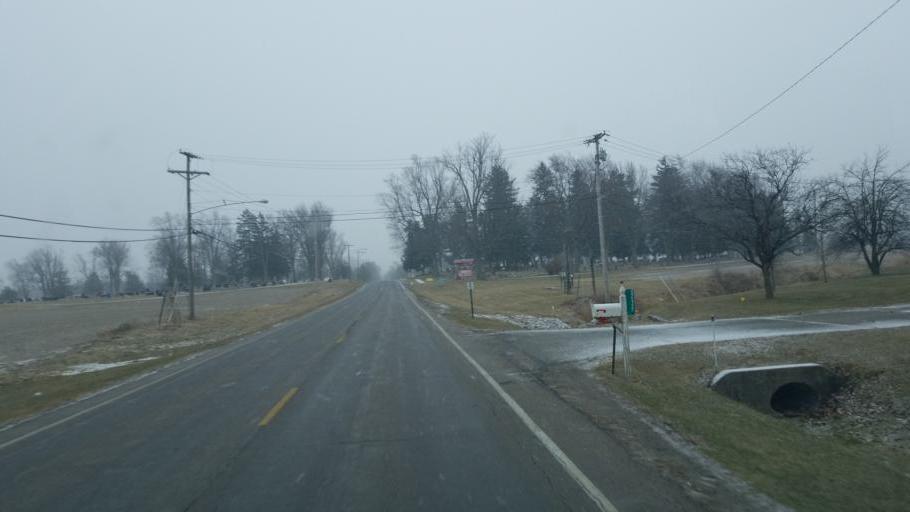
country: US
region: Ohio
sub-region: Defiance County
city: Hicksville
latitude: 41.3041
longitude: -84.7779
